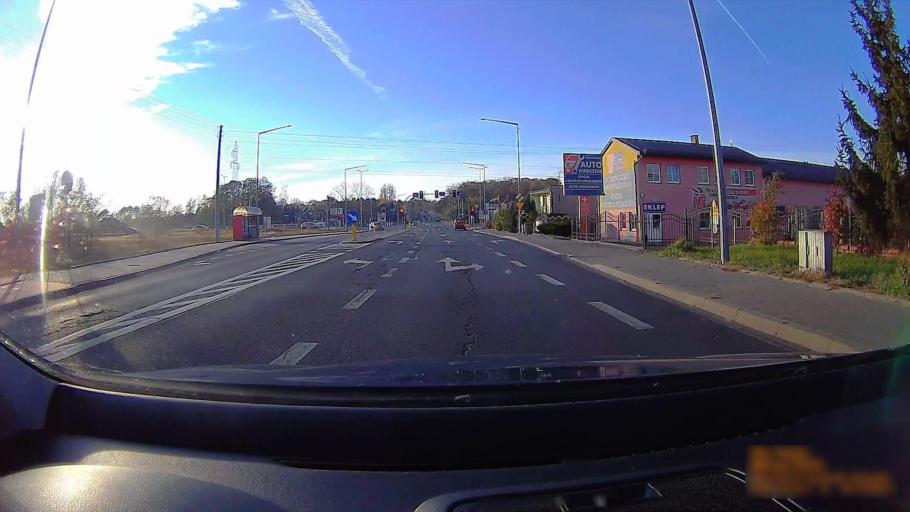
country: PL
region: Greater Poland Voivodeship
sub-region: Powiat koninski
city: Stare Miasto
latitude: 52.2029
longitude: 18.2274
